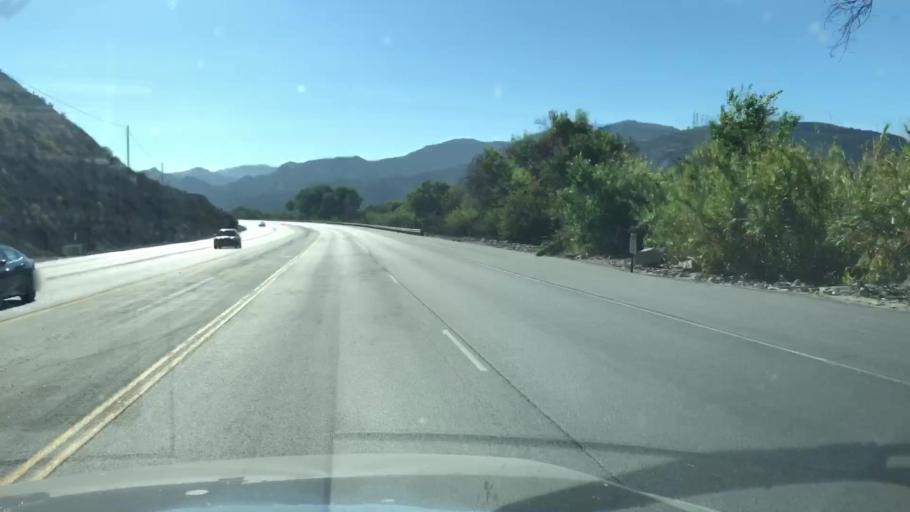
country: US
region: California
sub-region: Ventura County
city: Piru
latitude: 34.4069
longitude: -118.7218
